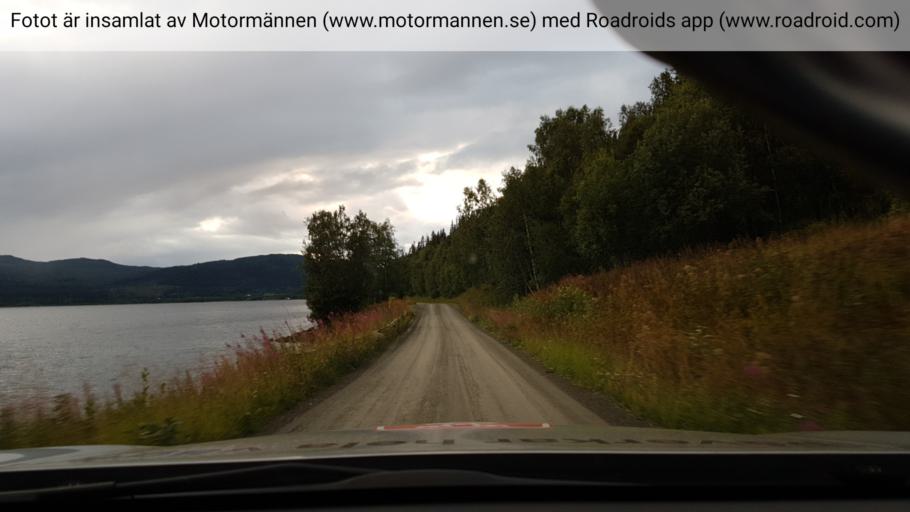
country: NO
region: Nordland
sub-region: Hattfjelldal
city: Hattfjelldal
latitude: 65.6439
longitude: 15.1928
